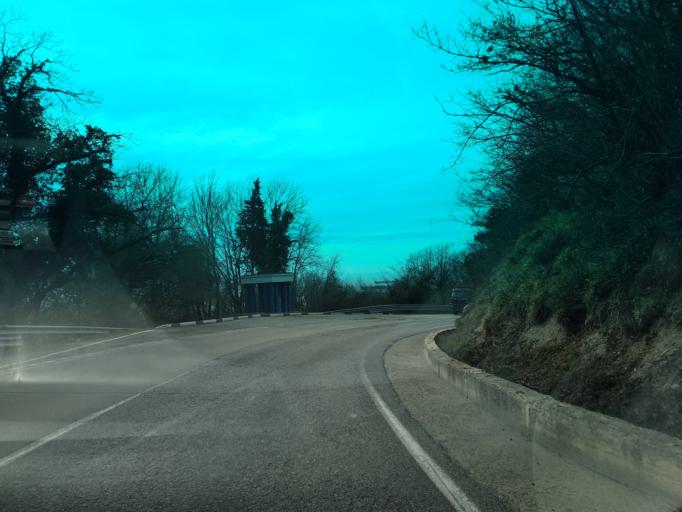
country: RU
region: Krasnodarskiy
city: Shepsi
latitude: 44.0436
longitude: 39.1390
